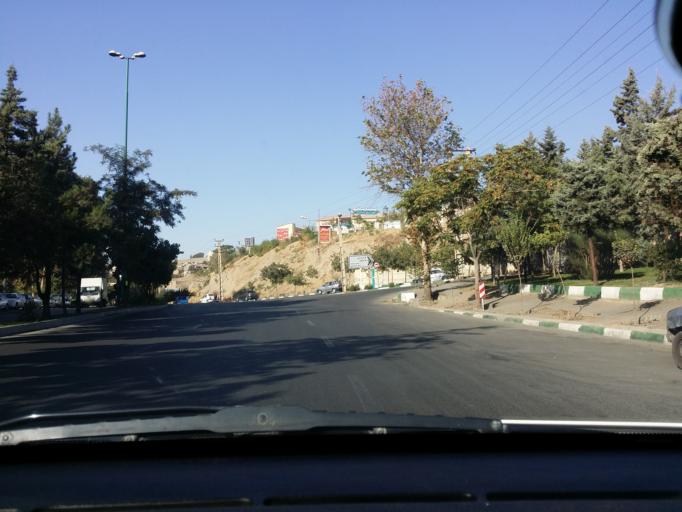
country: IR
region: Alborz
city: Karaj
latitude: 35.8284
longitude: 51.0236
